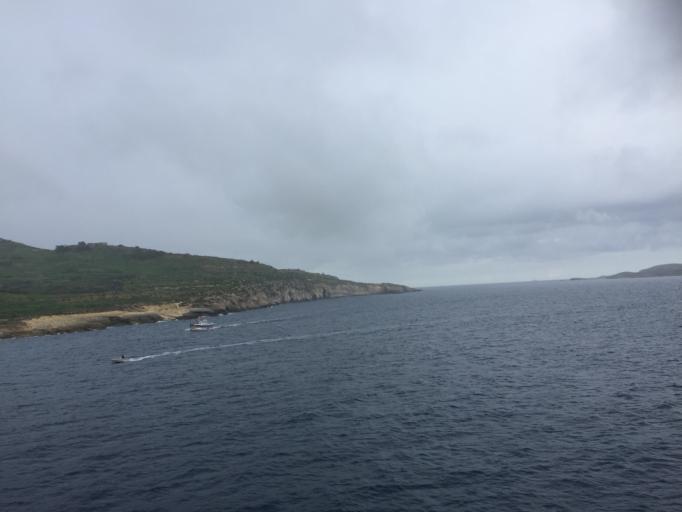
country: MT
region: Ghajnsielem
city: Mgarr
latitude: 36.0249
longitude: 14.3034
